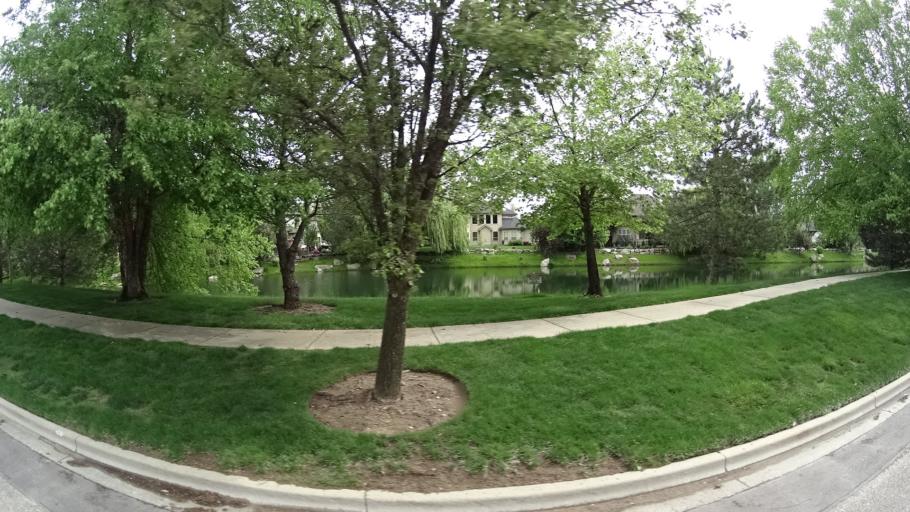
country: US
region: Idaho
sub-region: Ada County
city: Eagle
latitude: 43.6792
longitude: -116.3398
